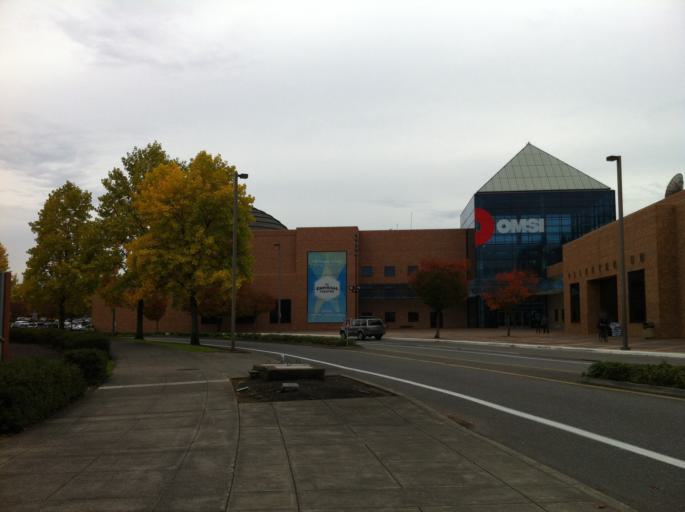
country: US
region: Oregon
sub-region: Multnomah County
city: Portland
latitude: 45.5093
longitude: -122.6657
